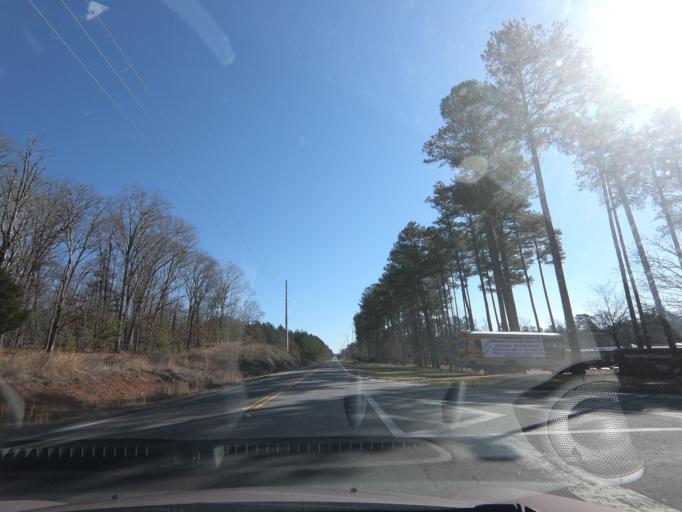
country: US
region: Georgia
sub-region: Dawson County
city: Dawsonville
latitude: 34.3538
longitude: -84.0836
